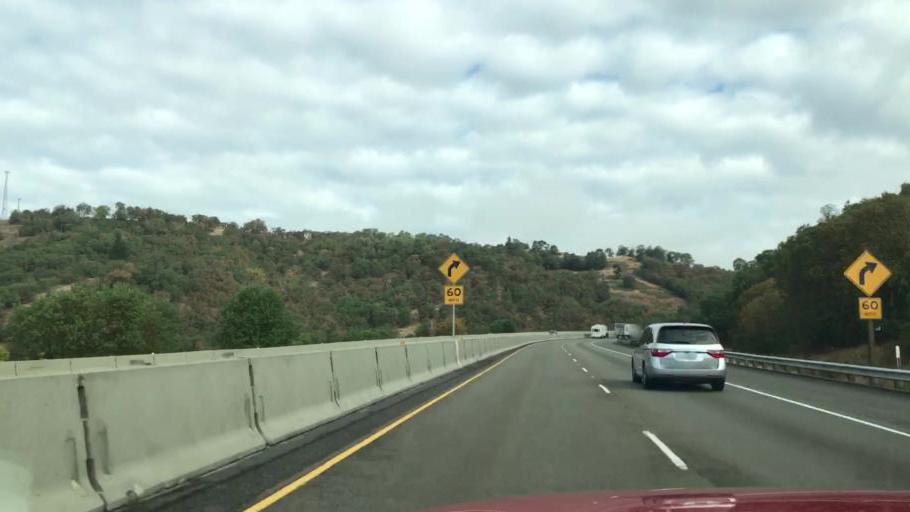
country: US
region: Oregon
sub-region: Douglas County
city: Winston
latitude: 43.1010
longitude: -123.3670
